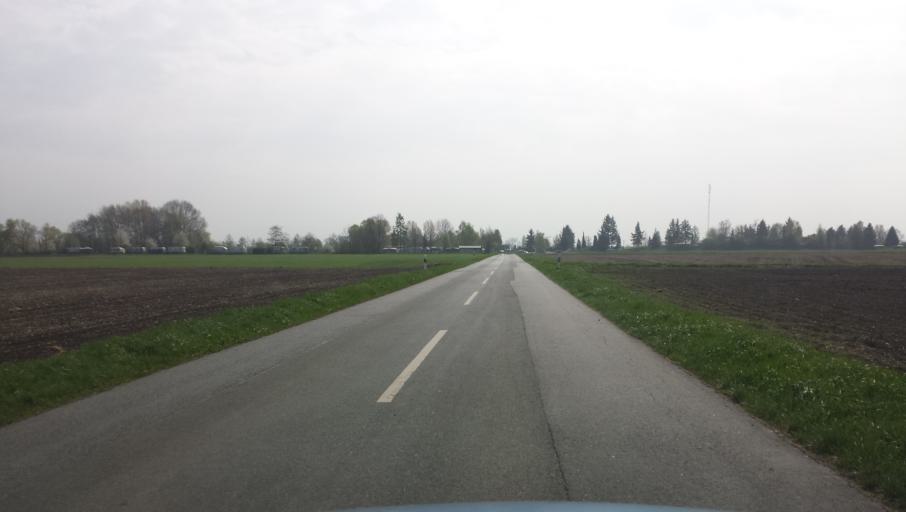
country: DE
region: Rheinland-Pfalz
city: Nierstein
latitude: 49.8808
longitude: 8.3768
